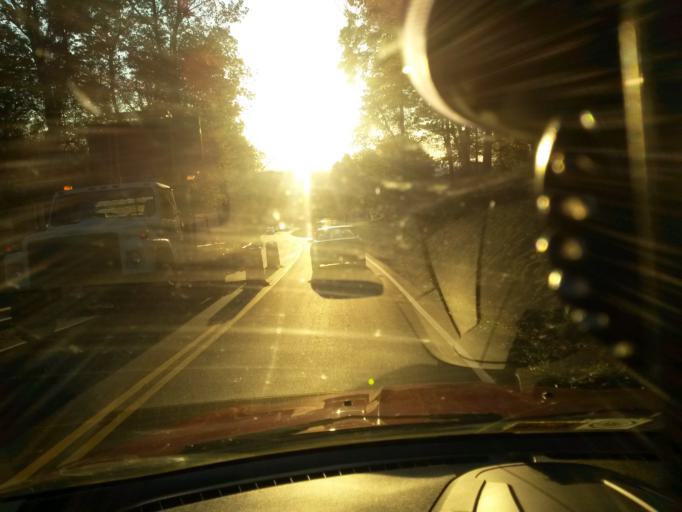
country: US
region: Virginia
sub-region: Roanoke County
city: Narrows
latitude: 37.1816
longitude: -79.8766
